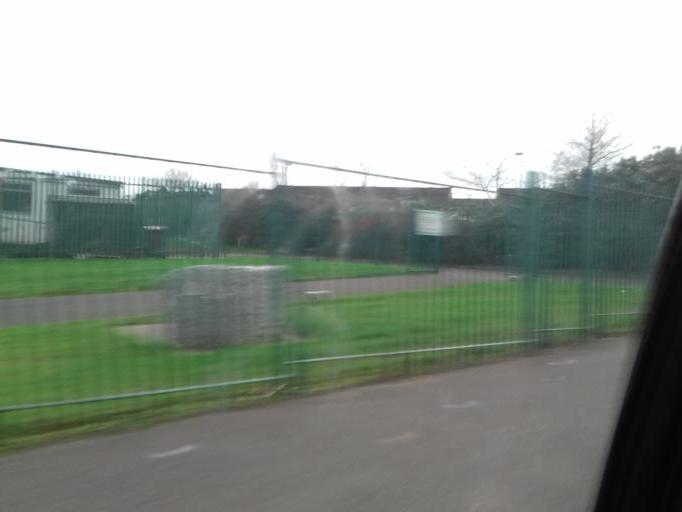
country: GB
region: Northern Ireland
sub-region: City of Belfast
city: Belfast
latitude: 54.6257
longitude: -5.9463
